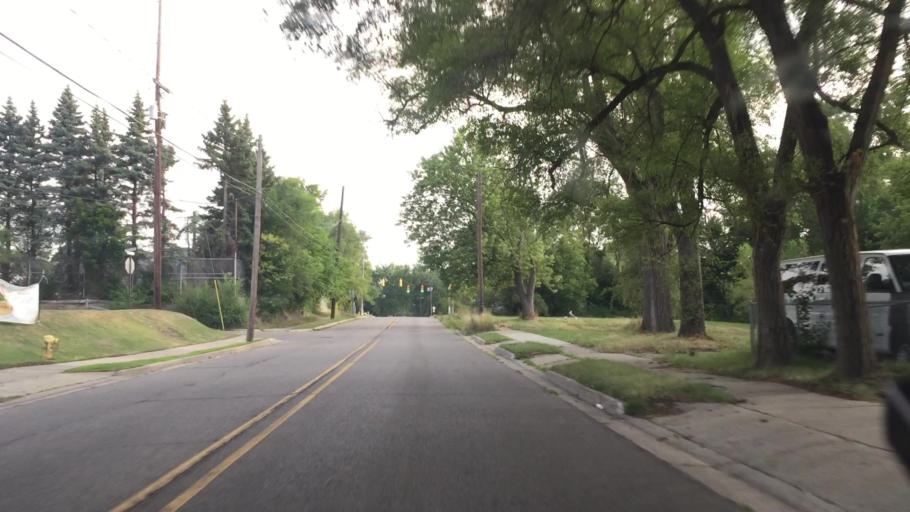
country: US
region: Michigan
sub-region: Oakland County
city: Pontiac
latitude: 42.6332
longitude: -83.2752
